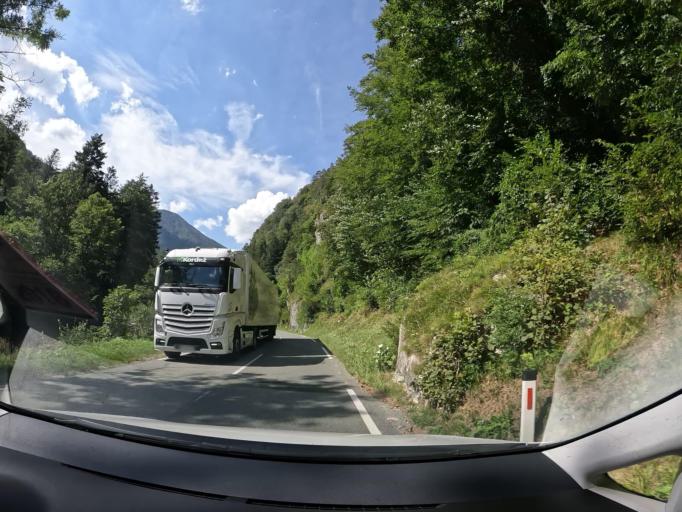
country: SI
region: Jezersko
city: Zgornje Jezersko
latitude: 46.3611
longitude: 14.4577
